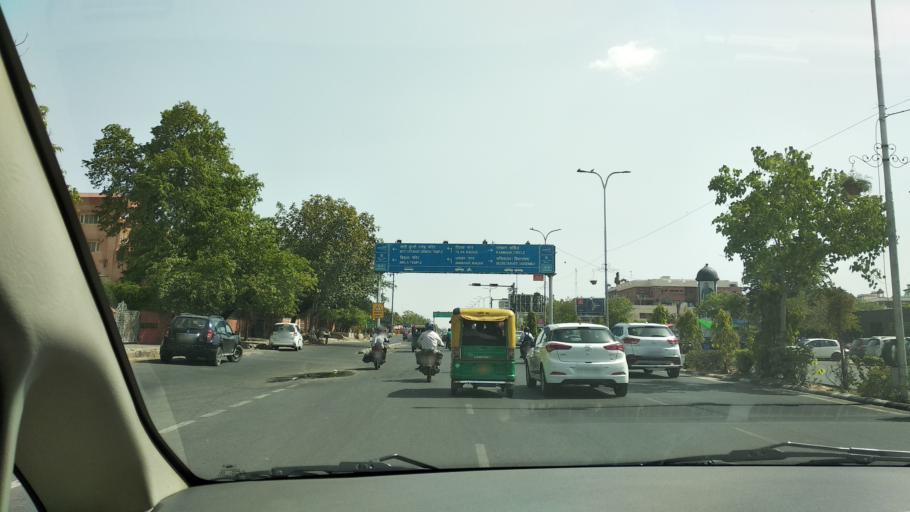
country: IN
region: Rajasthan
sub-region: Jaipur
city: Jaipur
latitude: 26.8959
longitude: 75.8155
